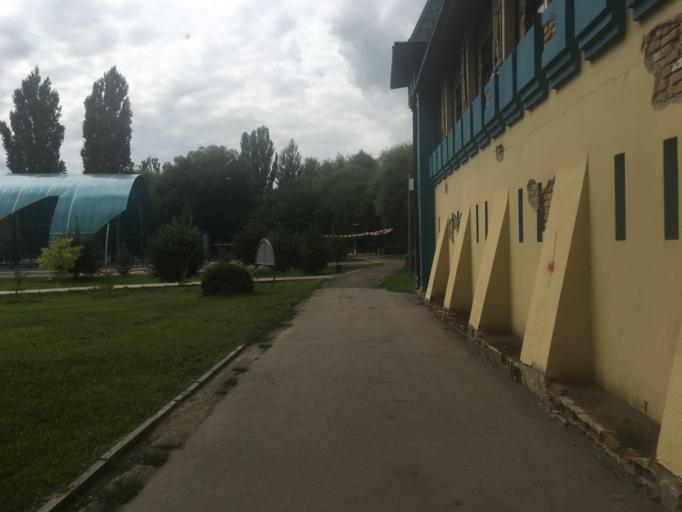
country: RU
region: Voronezj
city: Rossosh'
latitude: 50.1956
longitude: 39.5774
